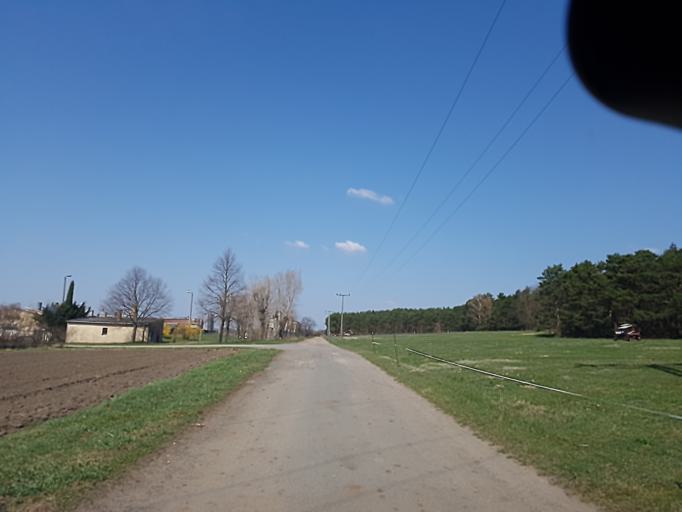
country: DE
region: Brandenburg
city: Trobitz
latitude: 51.5610
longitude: 13.4134
